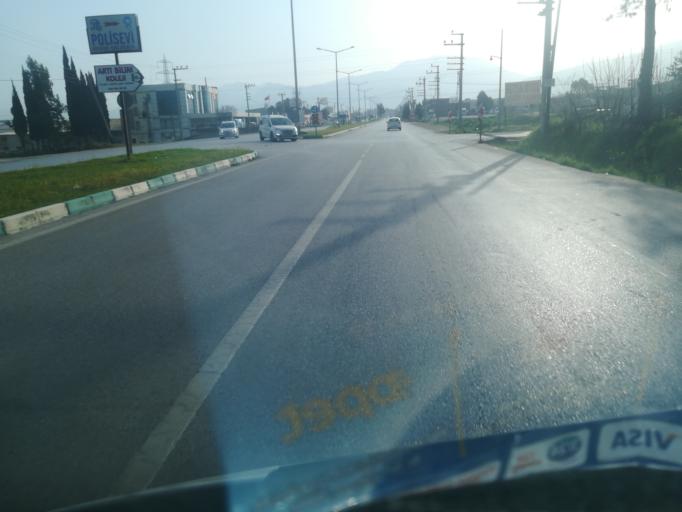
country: TR
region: Osmaniye
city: Toprakkale
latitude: 37.0561
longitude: 36.1918
